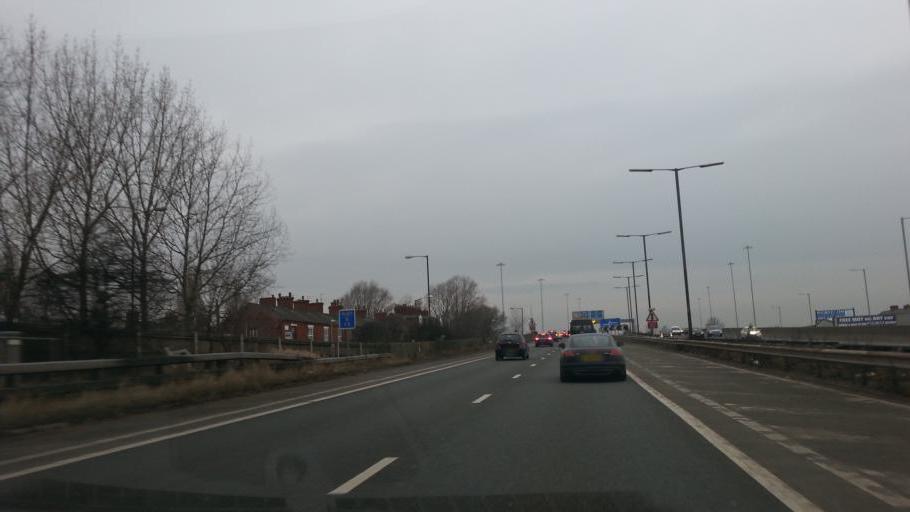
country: GB
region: England
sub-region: Borough of Tameside
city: Denton
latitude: 53.4564
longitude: -2.1263
